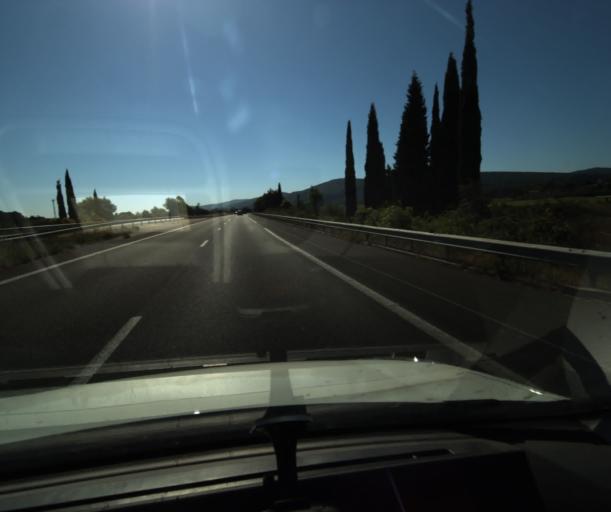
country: FR
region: Languedoc-Roussillon
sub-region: Departement de l'Aude
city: Trebes
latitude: 43.1930
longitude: 2.4517
